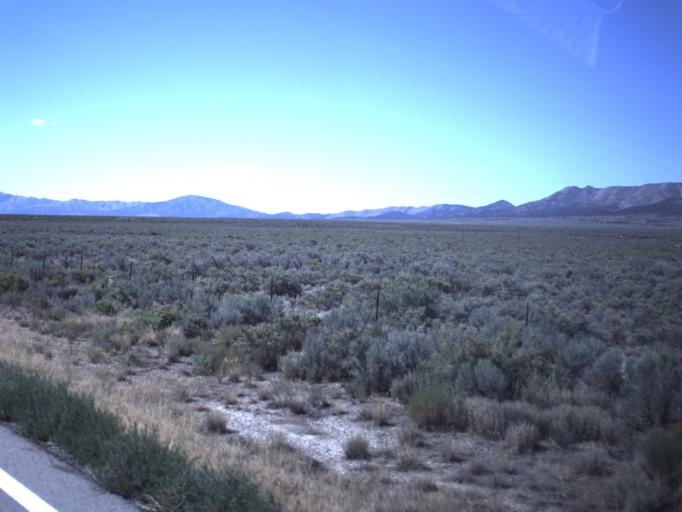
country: US
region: Utah
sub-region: Tooele County
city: Tooele
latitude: 40.2366
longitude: -112.4022
